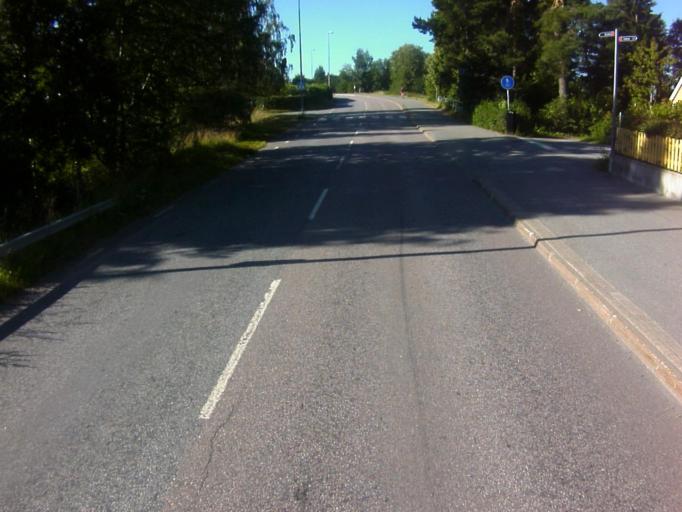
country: SE
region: Soedermanland
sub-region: Eskilstuna Kommun
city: Skogstorp
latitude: 59.3396
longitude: 16.4351
